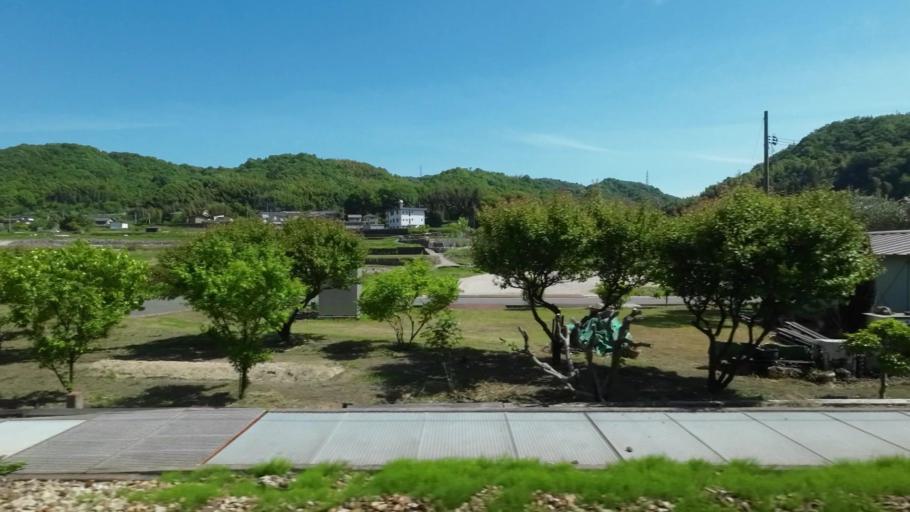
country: JP
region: Hiroshima
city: Fukuyama
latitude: 34.4637
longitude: 133.2900
